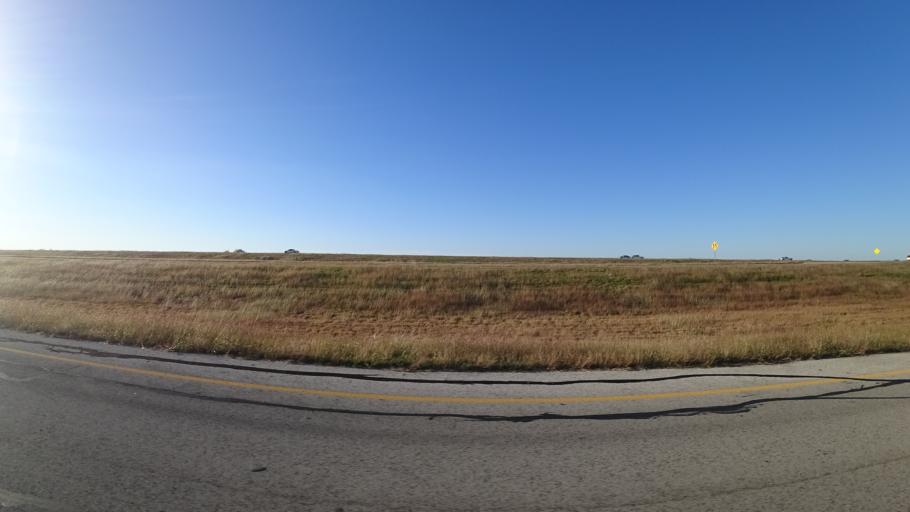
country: US
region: Texas
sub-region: Travis County
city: Onion Creek
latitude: 30.0892
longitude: -97.6812
